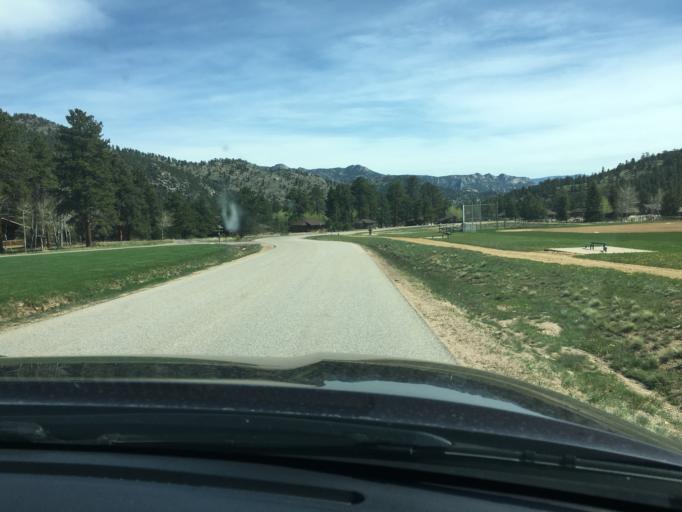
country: US
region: Colorado
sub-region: Larimer County
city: Estes Park
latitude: 40.3411
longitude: -105.5739
